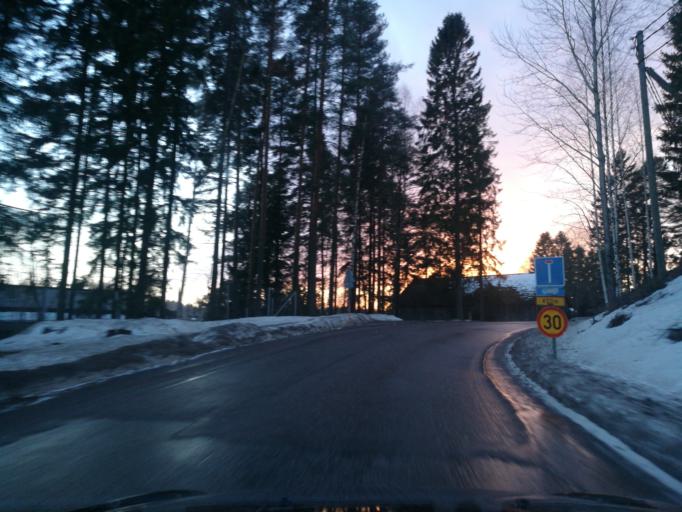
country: FI
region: Uusimaa
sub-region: Helsinki
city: Kerava
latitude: 60.3935
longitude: 25.1565
